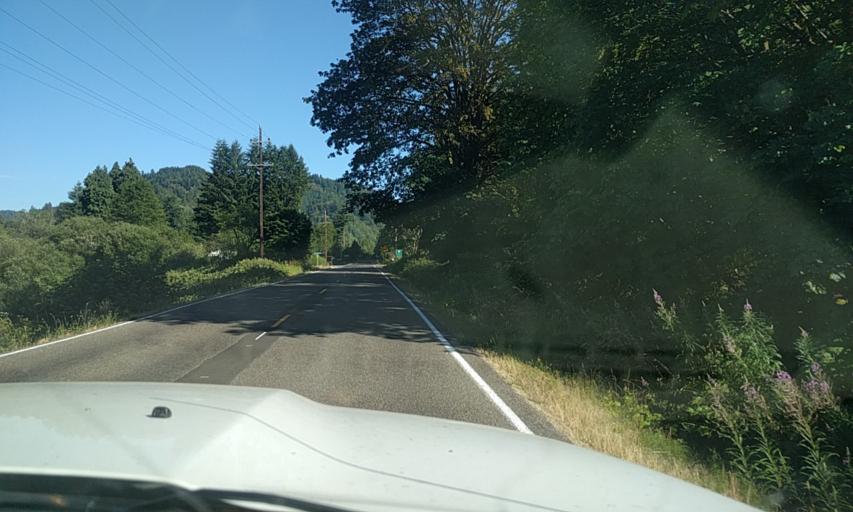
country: US
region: Oregon
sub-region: Lane County
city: Florence
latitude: 44.0384
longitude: -123.8659
